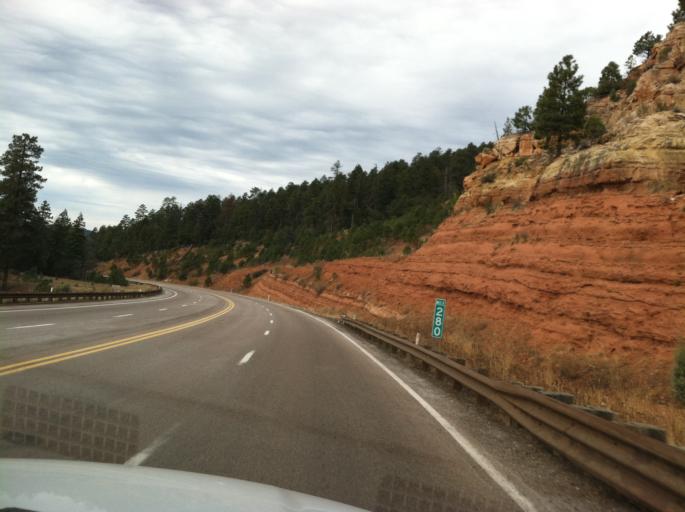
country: US
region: Arizona
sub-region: Gila County
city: Star Valley
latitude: 34.3071
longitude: -110.9311
